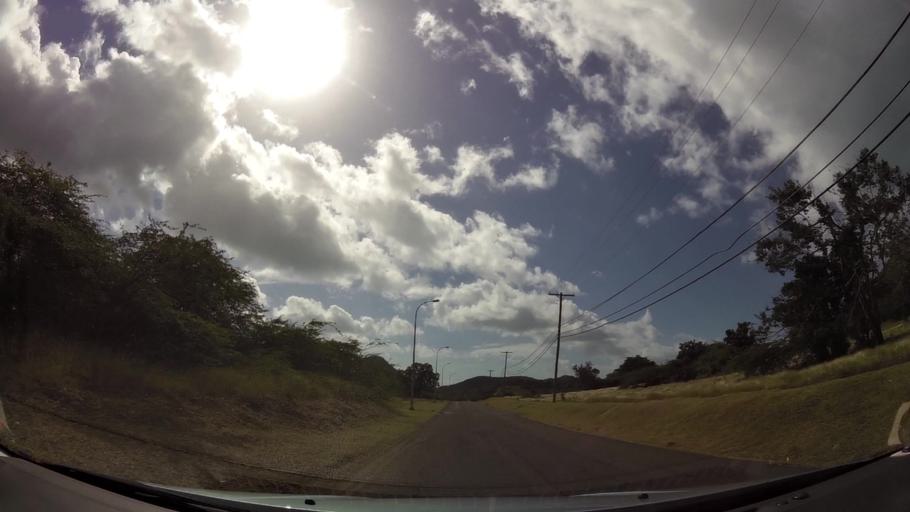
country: AG
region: Saint John
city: Saint John's
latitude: 17.1170
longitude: -61.8704
